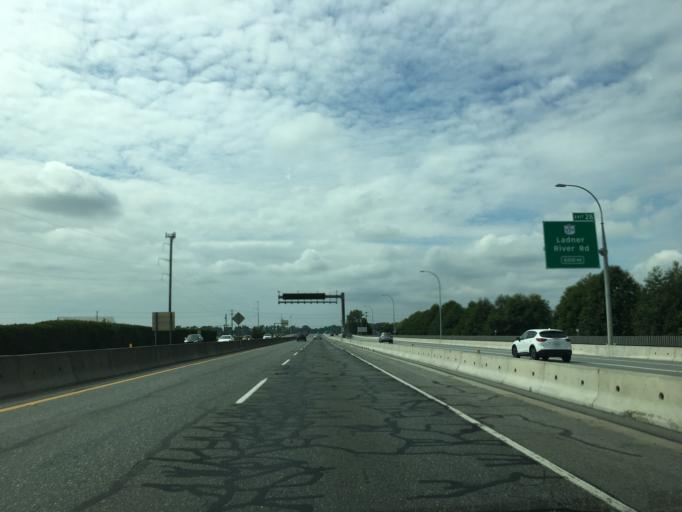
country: CA
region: British Columbia
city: Ladner
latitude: 49.1020
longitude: -123.0428
